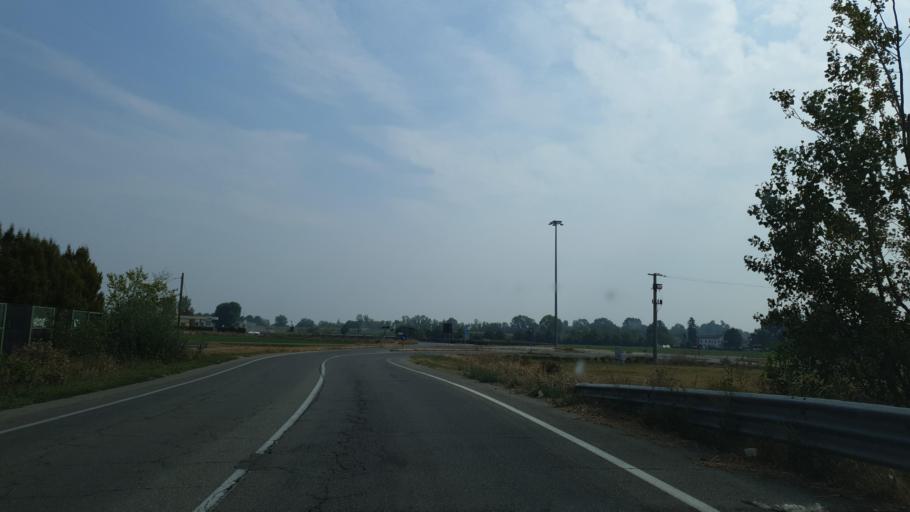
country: IT
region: Emilia-Romagna
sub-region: Provincia di Parma
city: San Secondo Parmense
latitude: 44.9189
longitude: 10.2443
